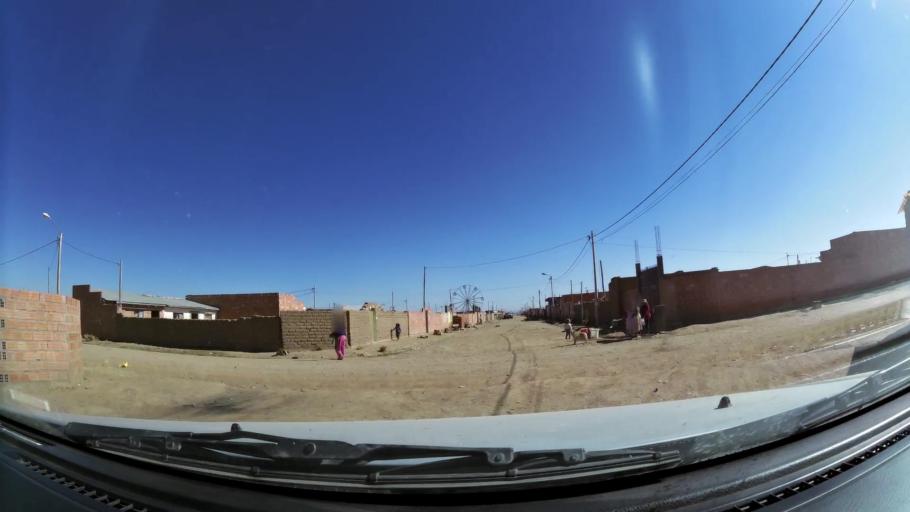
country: BO
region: La Paz
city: La Paz
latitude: -16.6131
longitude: -68.1963
